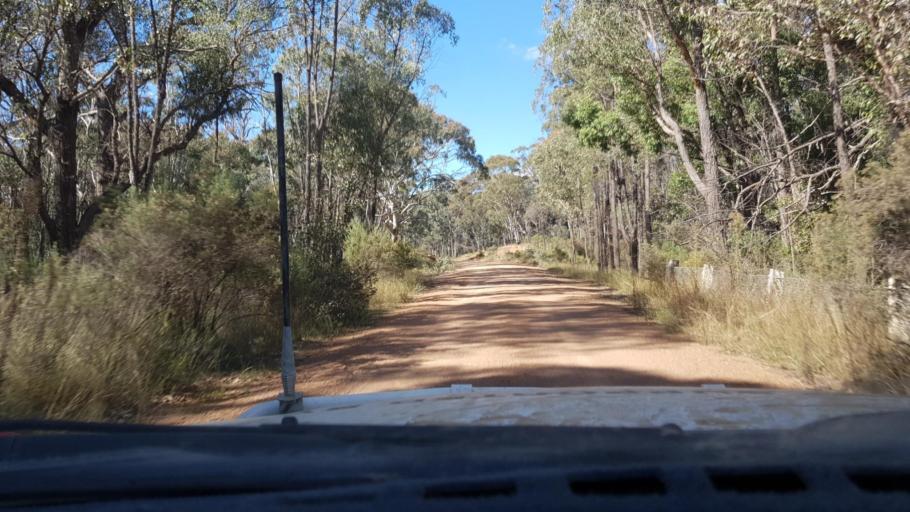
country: AU
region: New South Wales
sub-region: Tamworth Municipality
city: Manilla
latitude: -30.4566
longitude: 150.8816
